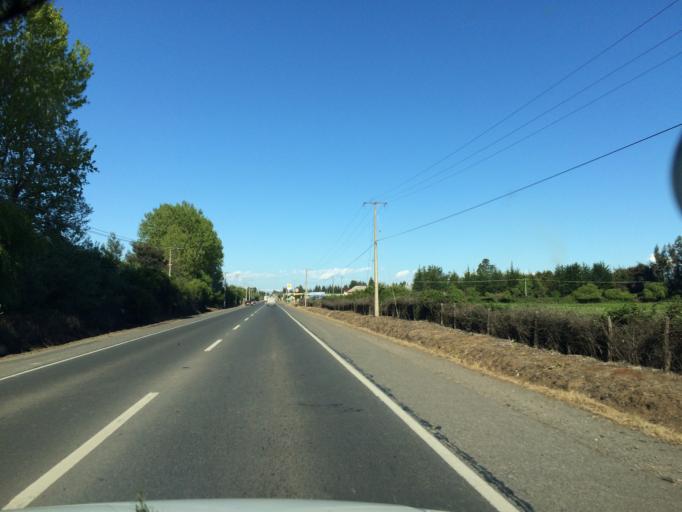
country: CL
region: Biobio
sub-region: Provincia de Biobio
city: Los Angeles
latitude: -37.4817
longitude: -72.4420
